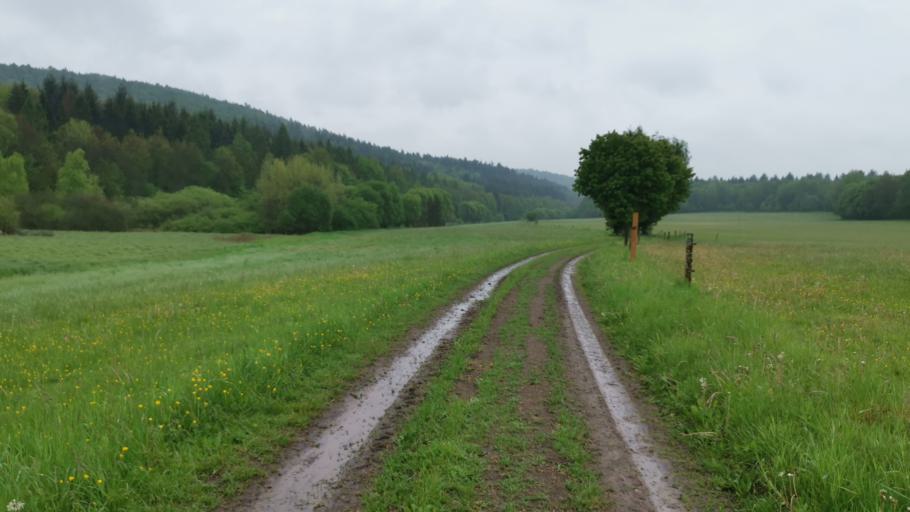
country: DE
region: Saarland
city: Kirkel
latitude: 49.2723
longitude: 7.1874
